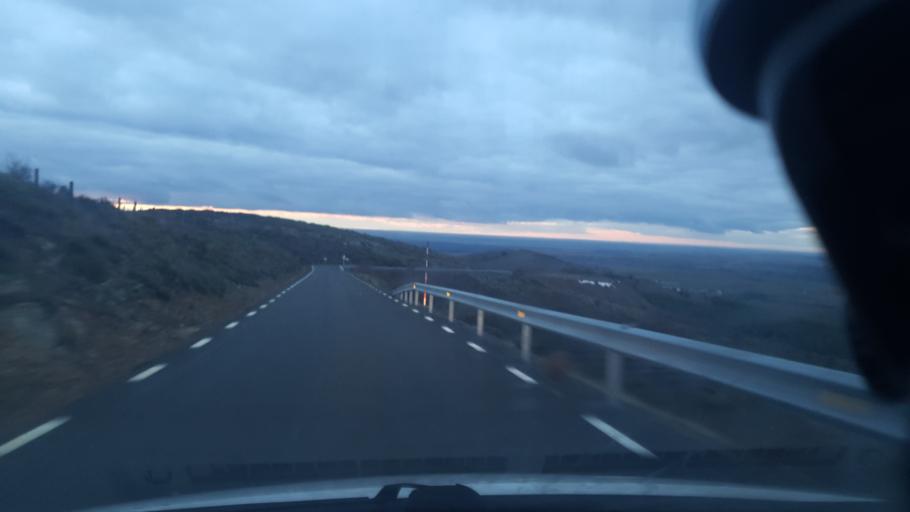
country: ES
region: Castille and Leon
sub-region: Provincia de Avila
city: Ojos-Albos
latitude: 40.7244
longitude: -4.4563
